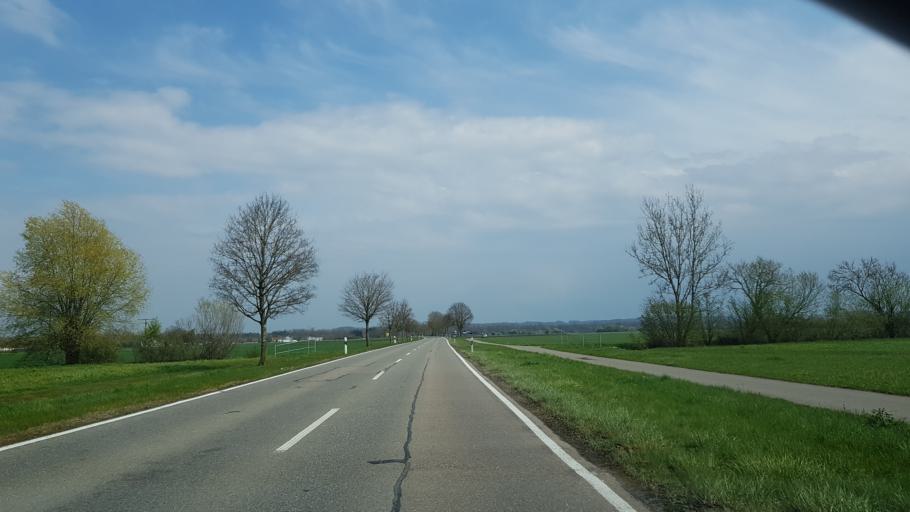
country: DE
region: Baden-Wuerttemberg
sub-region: Tuebingen Region
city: Dietenheim
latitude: 48.2035
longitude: 10.0598
